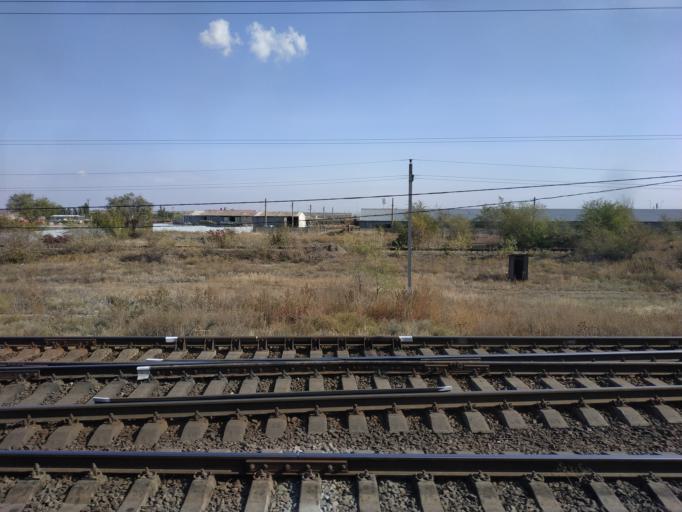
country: RU
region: Volgograd
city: Gumrak
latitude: 48.7901
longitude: 44.3680
